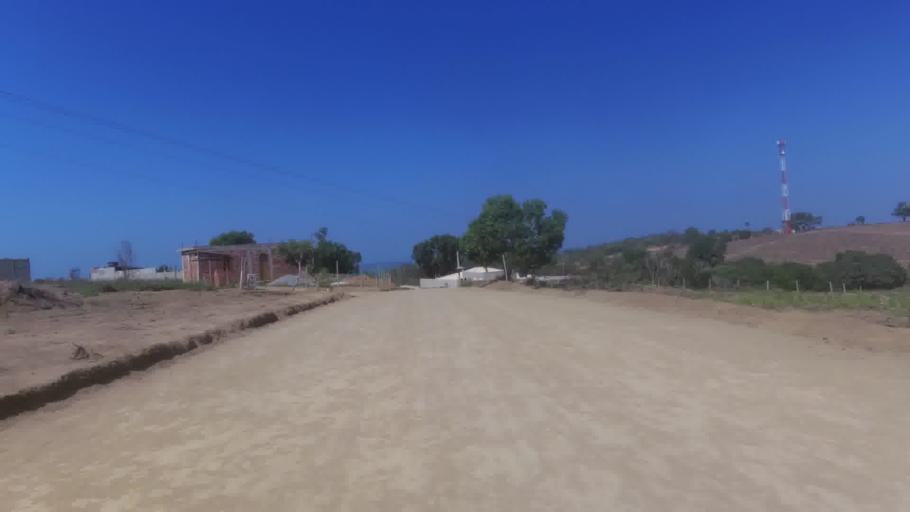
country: BR
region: Espirito Santo
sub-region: Marataizes
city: Marataizes
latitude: -21.1106
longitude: -40.8572
